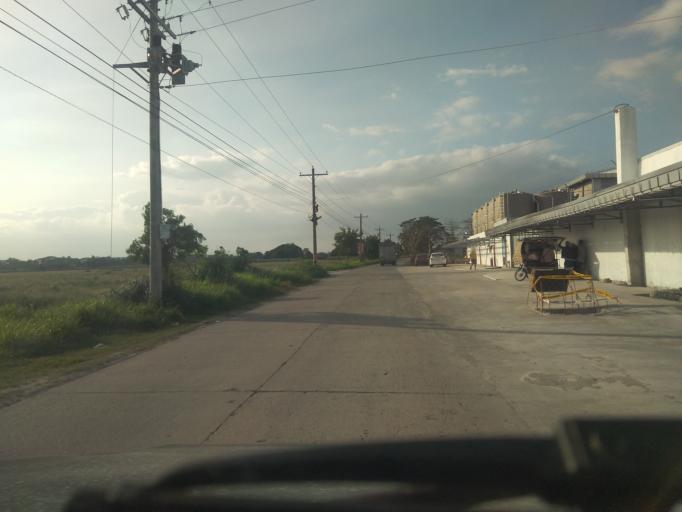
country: PH
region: Central Luzon
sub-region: Province of Pampanga
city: Malino
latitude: 15.1066
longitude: 120.6724
